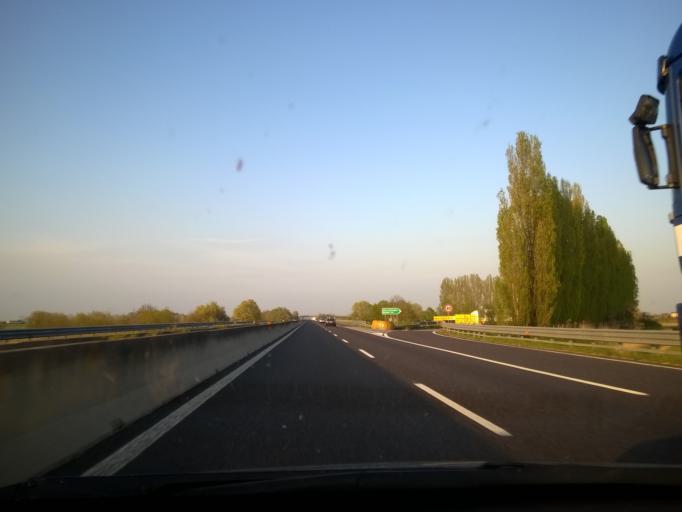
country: IT
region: Veneto
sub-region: Provincia di Rovigo
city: Fiesso Umbertiano
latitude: 44.9331
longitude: 11.6091
